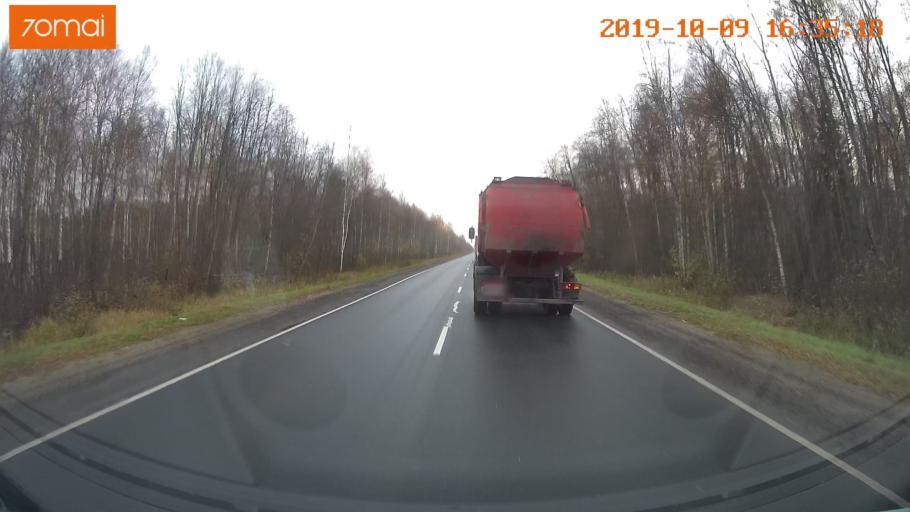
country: RU
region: Kostroma
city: Oktyabr'skiy
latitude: 57.5572
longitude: 40.9996
